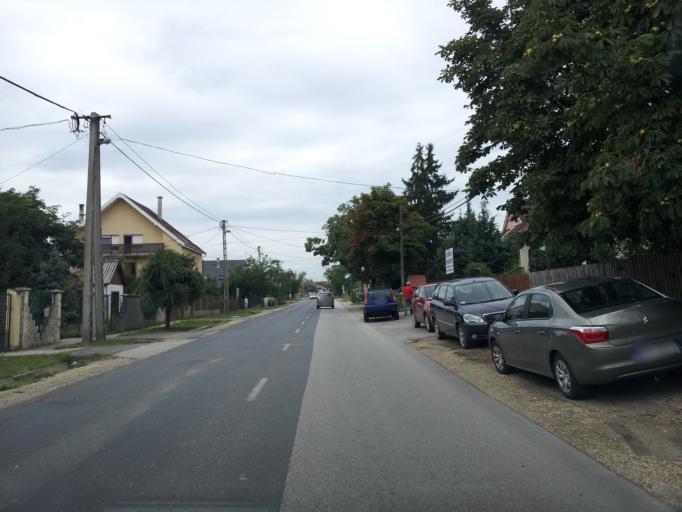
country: HU
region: Pest
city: Erd
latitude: 47.3873
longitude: 18.9017
